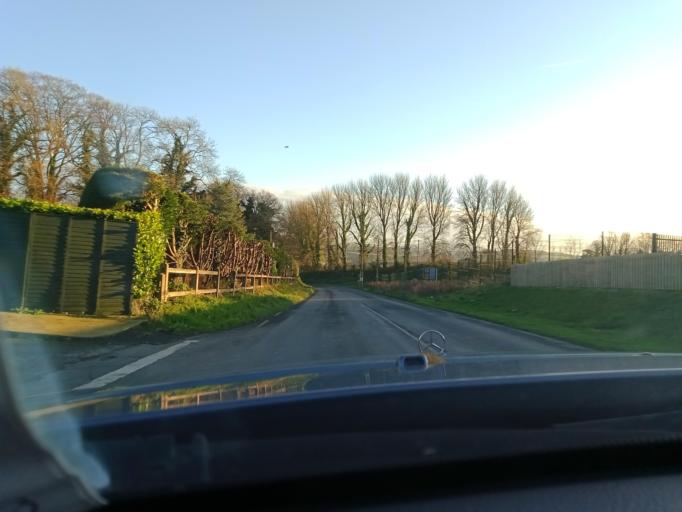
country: IE
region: Leinster
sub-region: Loch Garman
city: New Ross
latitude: 52.3961
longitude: -6.9577
